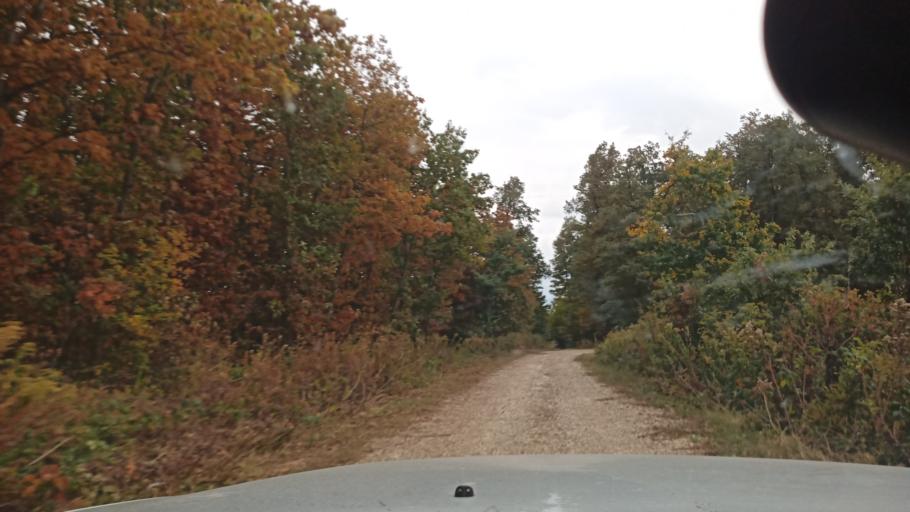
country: HU
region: Fejer
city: Bodajk
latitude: 47.3745
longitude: 18.2757
